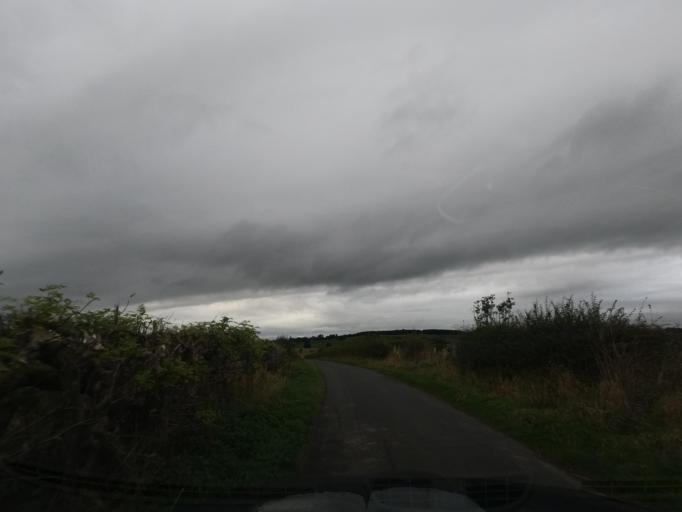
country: GB
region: England
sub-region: Northumberland
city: Ford
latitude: 55.6179
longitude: -2.0757
